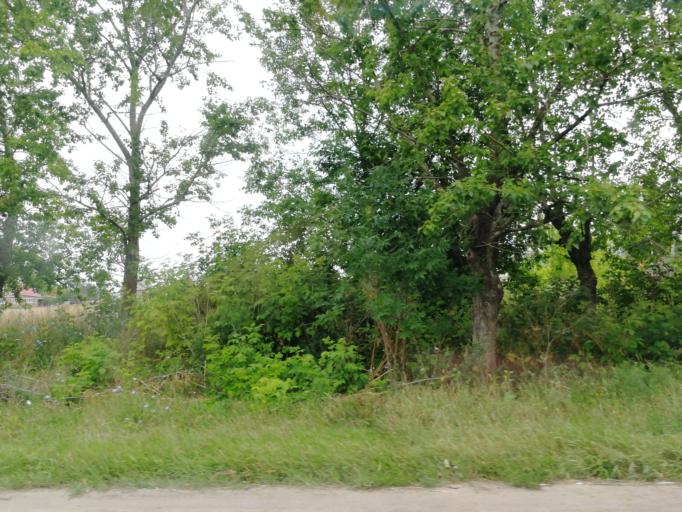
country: RU
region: Tula
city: Tovarkovskiy
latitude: 53.6884
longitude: 38.1844
